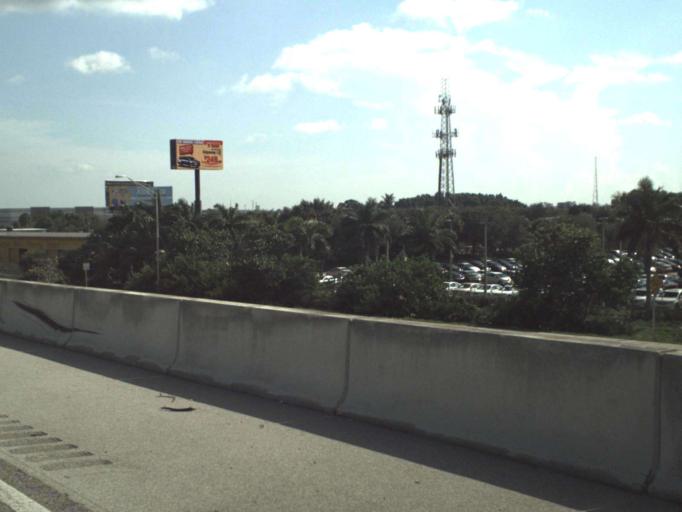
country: US
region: Florida
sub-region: Palm Beach County
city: Mangonia Park
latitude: 26.7841
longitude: -80.0989
